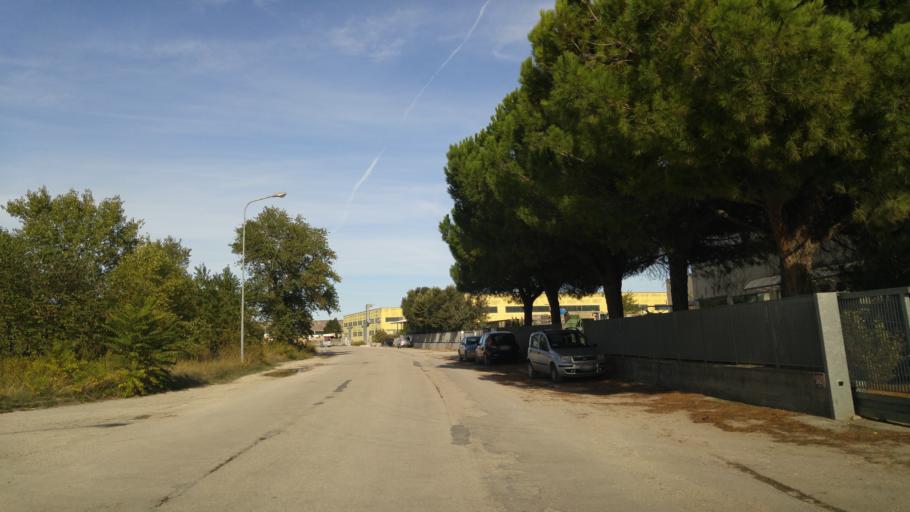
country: IT
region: The Marches
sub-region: Provincia di Pesaro e Urbino
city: Bellocchi
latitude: 43.7865
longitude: 13.0097
